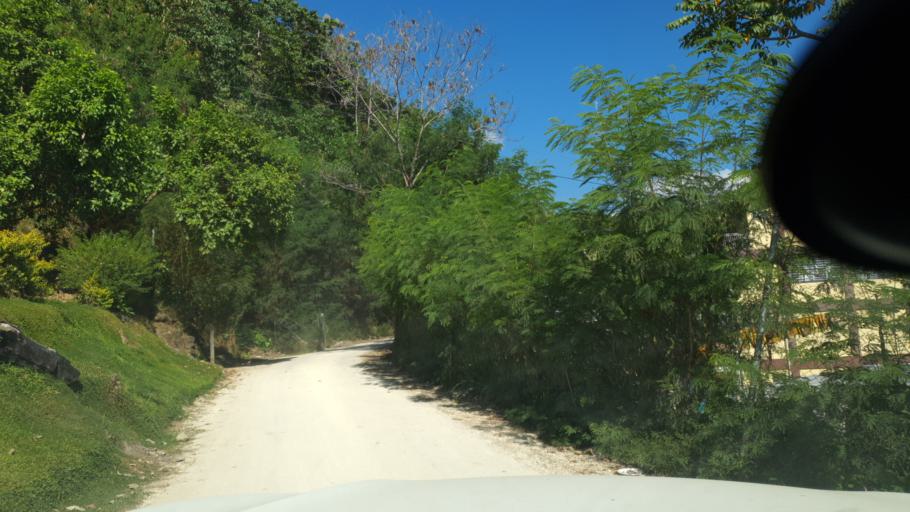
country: SB
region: Guadalcanal
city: Honiara
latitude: -9.4387
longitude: 159.9693
